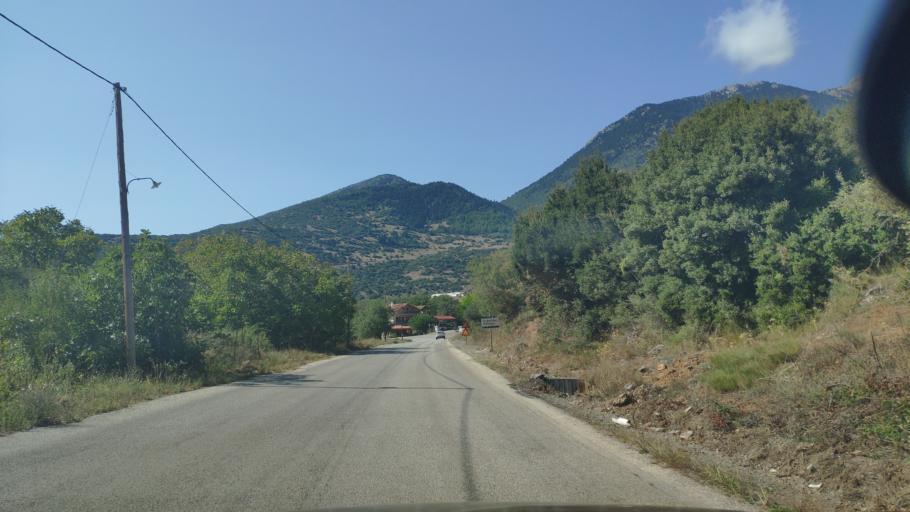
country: GR
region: Peloponnese
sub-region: Nomos Korinthias
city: Nemea
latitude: 37.9241
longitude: 22.5281
